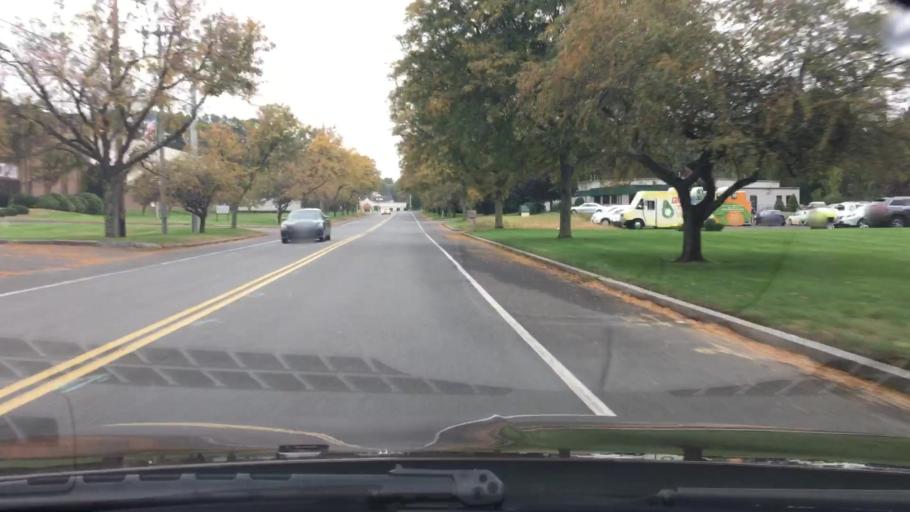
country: US
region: Massachusetts
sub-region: Hampden County
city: East Longmeadow
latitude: 42.0454
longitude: -72.5323
